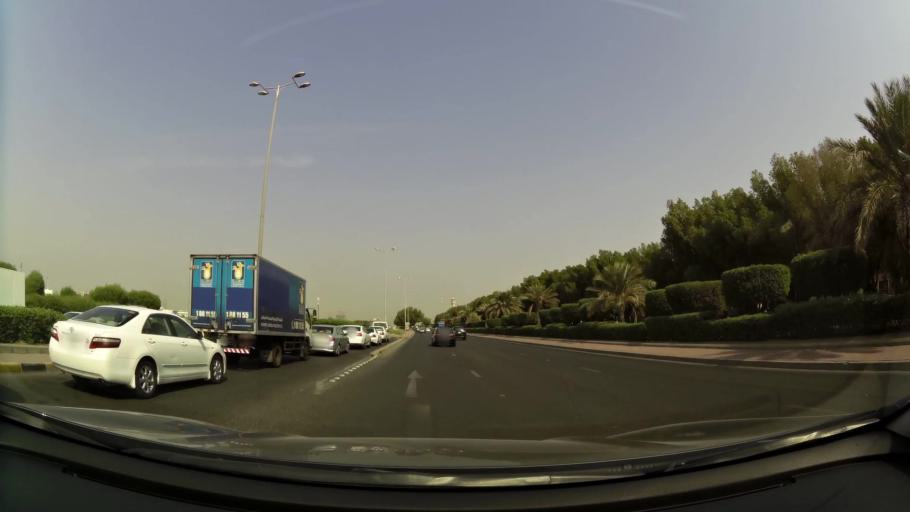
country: KW
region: Al Asimah
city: Ar Rabiyah
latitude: 29.2915
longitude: 47.9283
